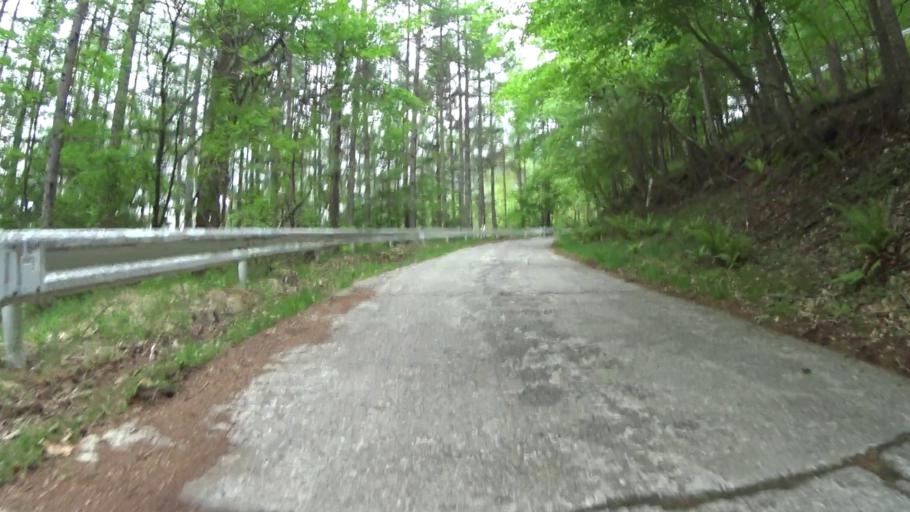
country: JP
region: Yamanashi
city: Kofu-shi
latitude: 35.8344
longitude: 138.5686
